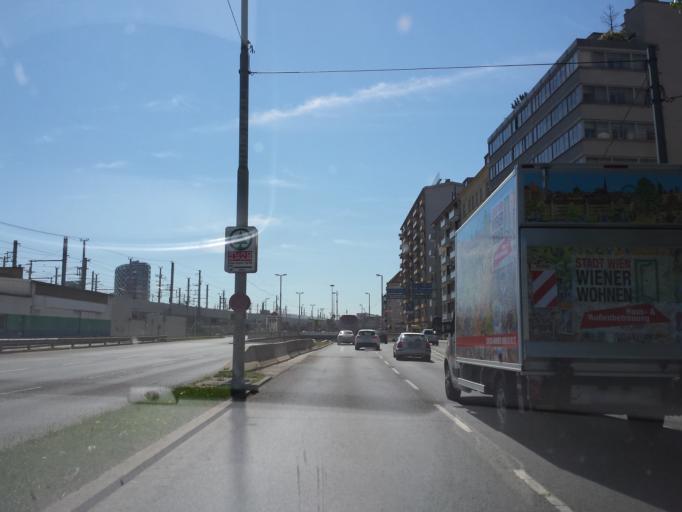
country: AT
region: Vienna
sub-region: Wien Stadt
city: Vienna
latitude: 48.1819
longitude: 16.3616
